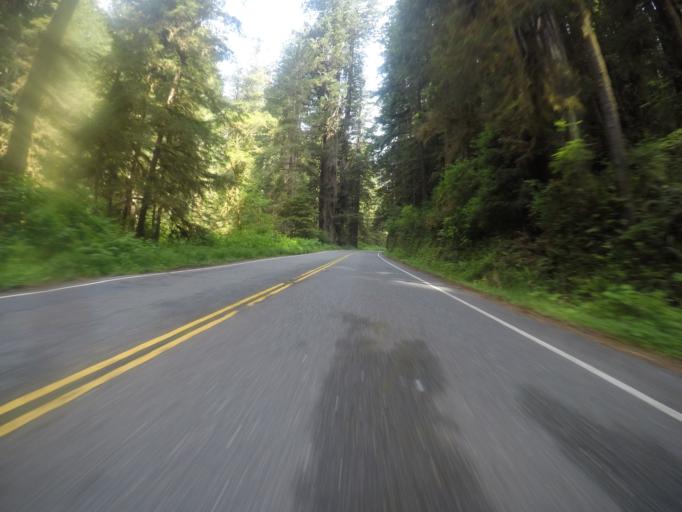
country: US
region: California
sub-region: Del Norte County
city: Bertsch-Oceanview
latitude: 41.4350
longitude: -124.0393
